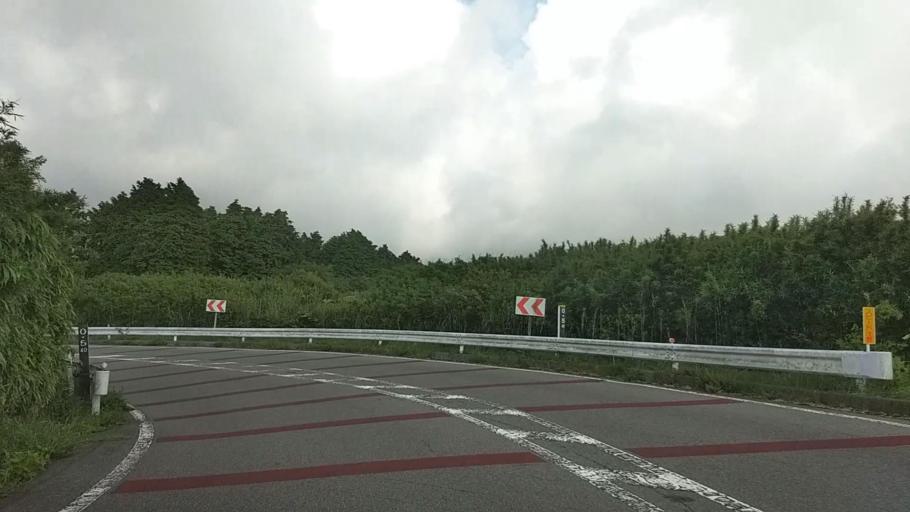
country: JP
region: Kanagawa
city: Hakone
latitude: 35.1824
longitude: 139.0106
